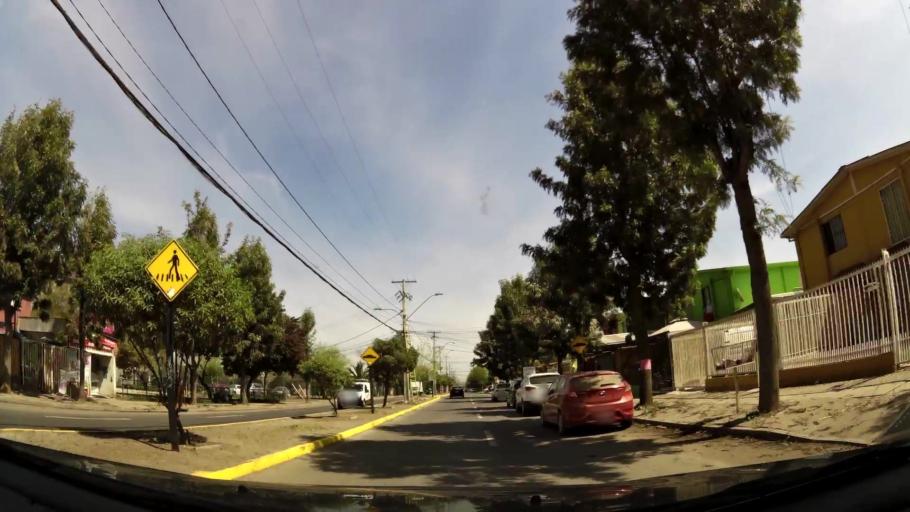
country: CL
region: Santiago Metropolitan
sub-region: Provincia de Cordillera
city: Puente Alto
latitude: -33.6139
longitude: -70.5520
